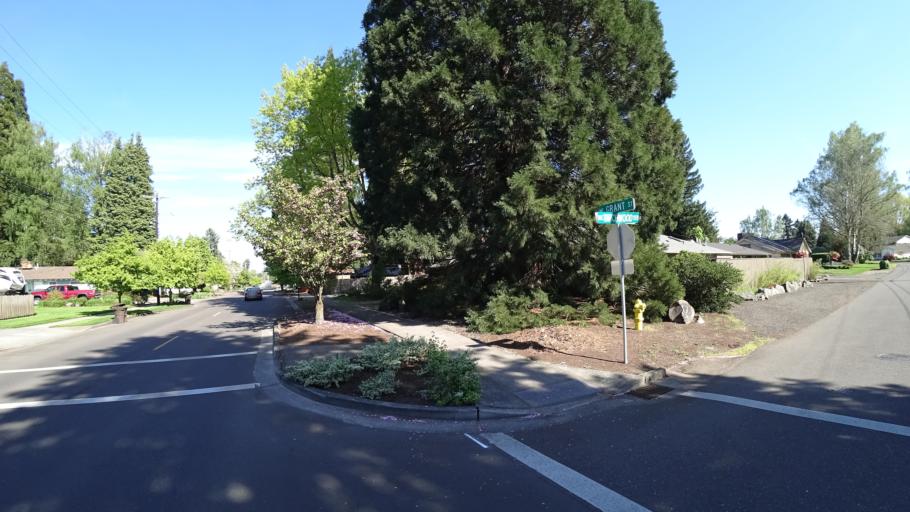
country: US
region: Oregon
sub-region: Washington County
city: Hillsboro
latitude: 45.5283
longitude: -122.9785
